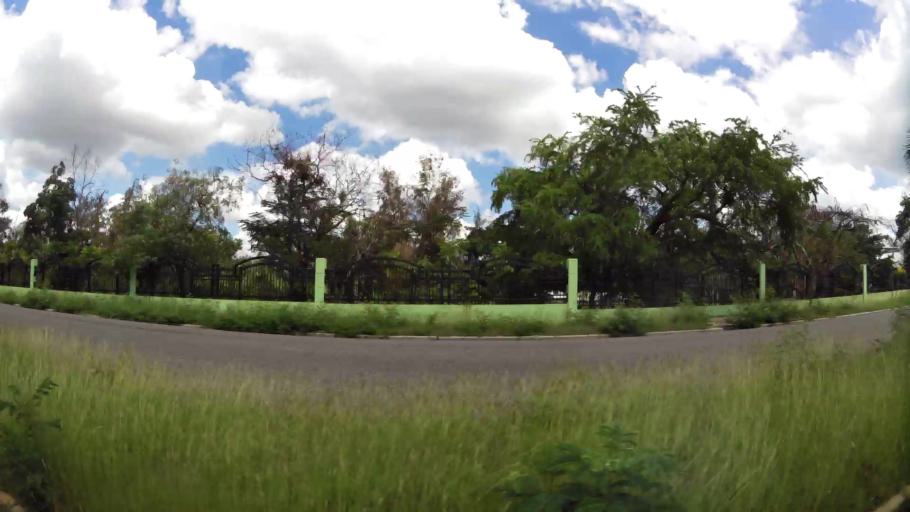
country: DO
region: Santo Domingo
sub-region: Santo Domingo
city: Santo Domingo Este
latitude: 18.4779
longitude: -69.8576
